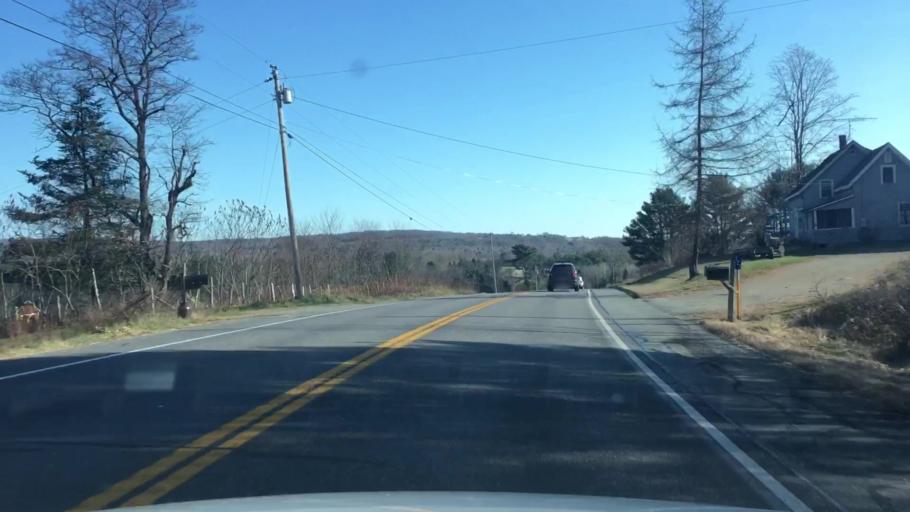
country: US
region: Maine
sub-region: Knox County
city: Washington
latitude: 44.2413
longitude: -69.3707
